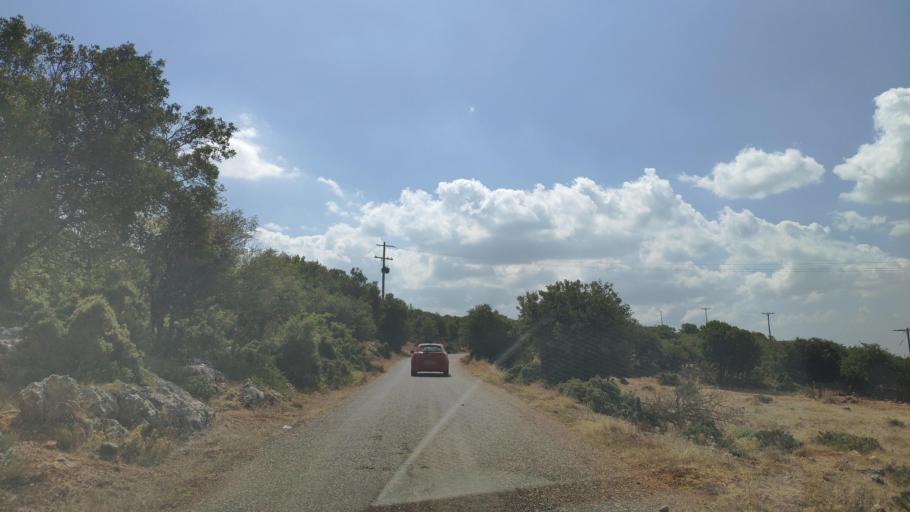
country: GR
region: Peloponnese
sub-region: Nomos Lakonias
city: Kariai
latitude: 37.3053
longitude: 22.4576
